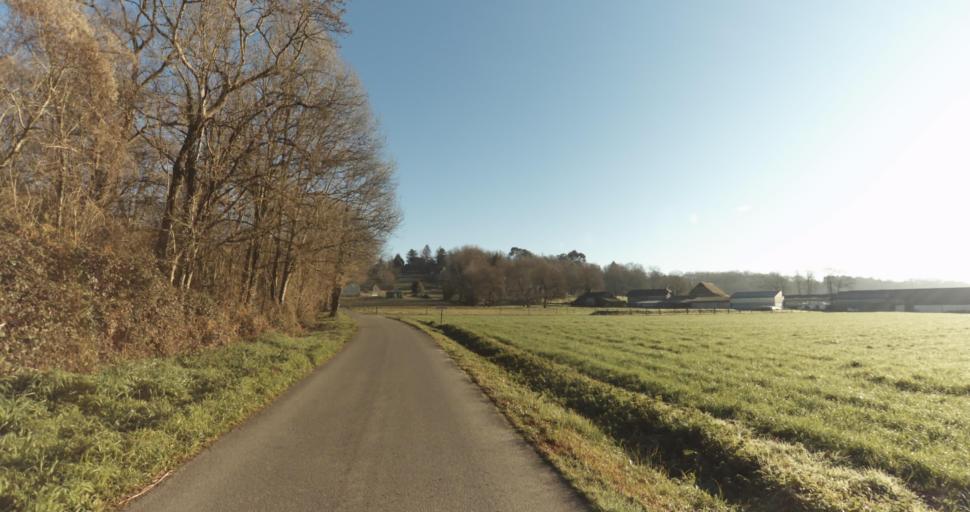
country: FR
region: Aquitaine
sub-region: Departement des Pyrenees-Atlantiques
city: Ousse
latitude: 43.3122
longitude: -0.2489
